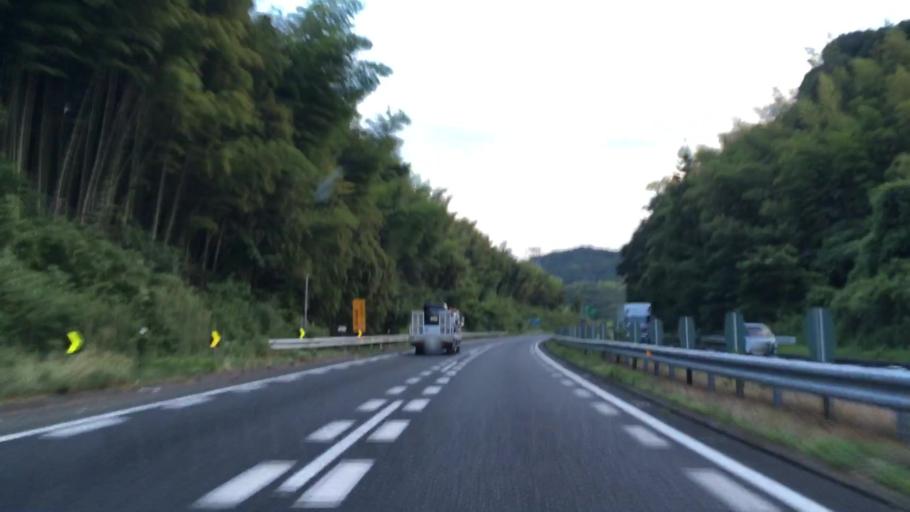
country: JP
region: Yamaguchi
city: Shimonoseki
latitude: 33.9345
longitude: 130.9962
